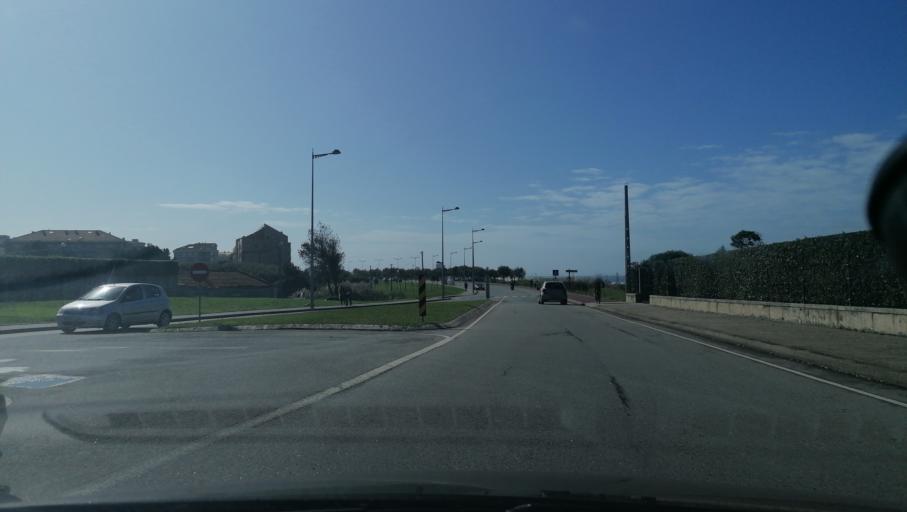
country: PT
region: Aveiro
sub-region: Espinho
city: Espinho
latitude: 41.0273
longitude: -8.6426
